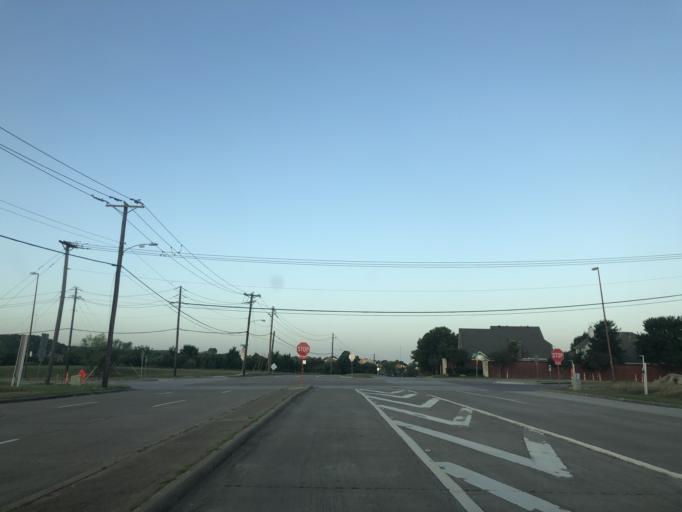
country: US
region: Texas
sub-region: Dallas County
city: Duncanville
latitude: 32.6496
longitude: -96.9641
